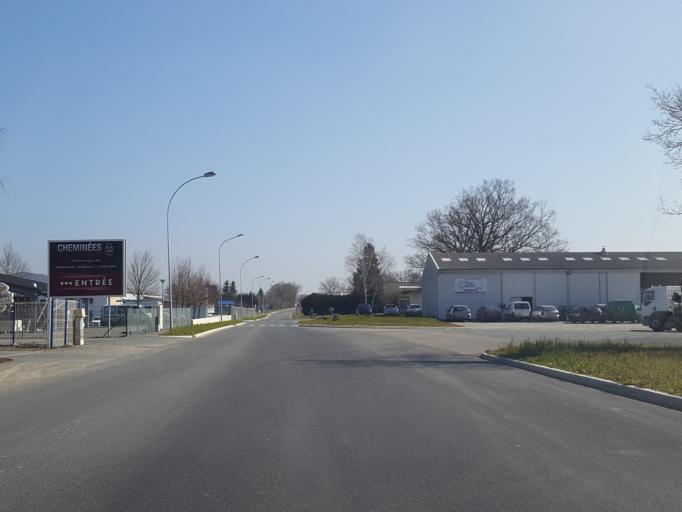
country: FR
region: Pays de la Loire
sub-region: Departement de la Vendee
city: La Chaize-le-Vicomte
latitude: 46.6665
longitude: -1.3359
